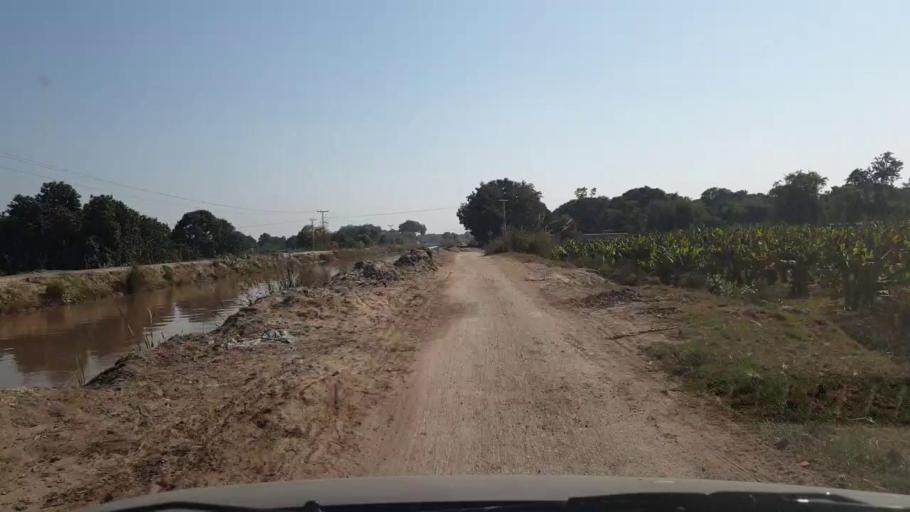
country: PK
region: Sindh
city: Tando Allahyar
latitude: 25.4477
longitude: 68.6341
